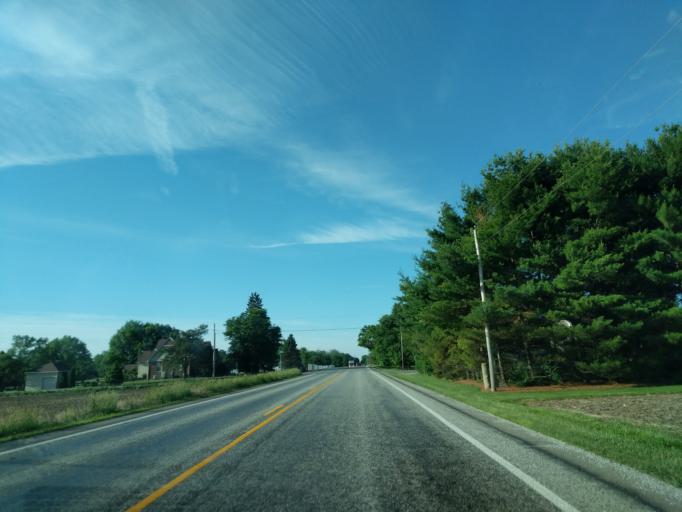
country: US
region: Indiana
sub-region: Madison County
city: Ingalls
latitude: 39.9164
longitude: -85.7709
